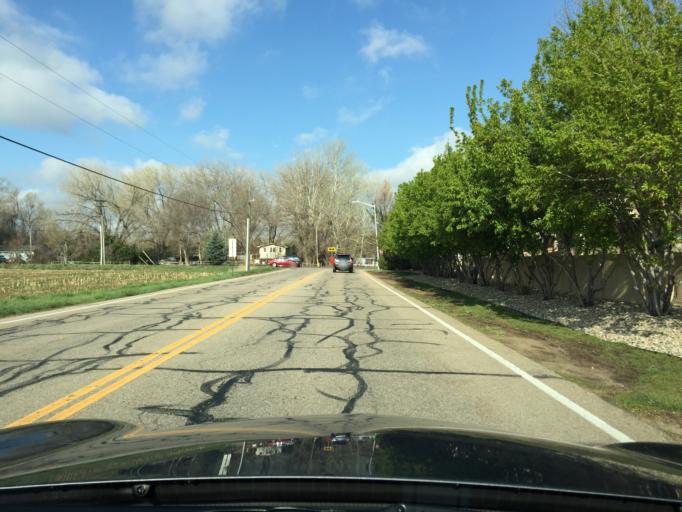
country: US
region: Colorado
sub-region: Boulder County
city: Longmont
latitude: 40.1307
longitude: -105.1299
